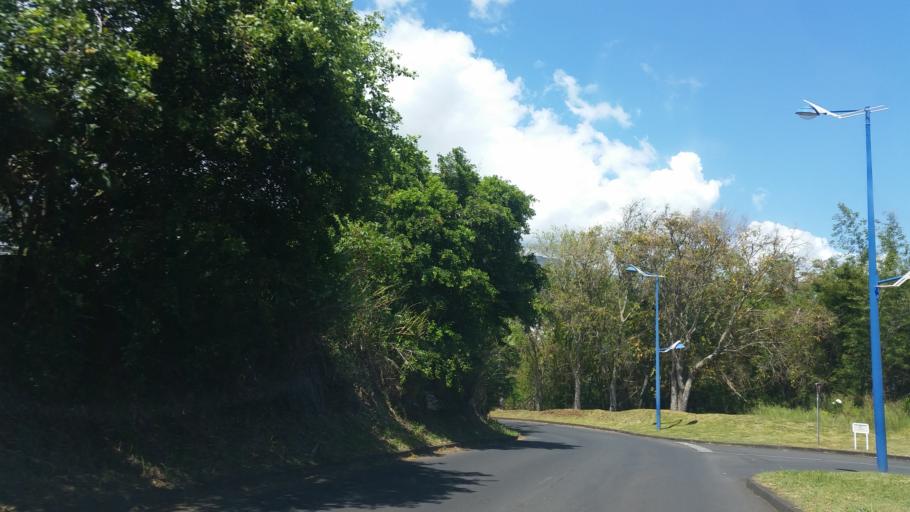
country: RE
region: Reunion
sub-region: Reunion
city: Sainte-Marie
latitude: -20.9250
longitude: 55.5280
